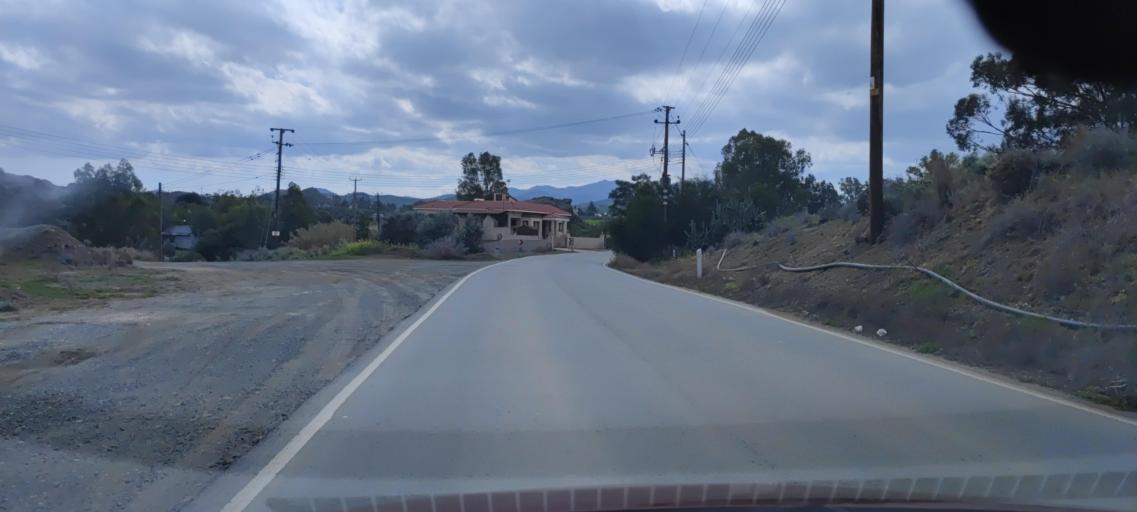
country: CY
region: Lefkosia
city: Pera
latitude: 35.0163
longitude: 33.2962
